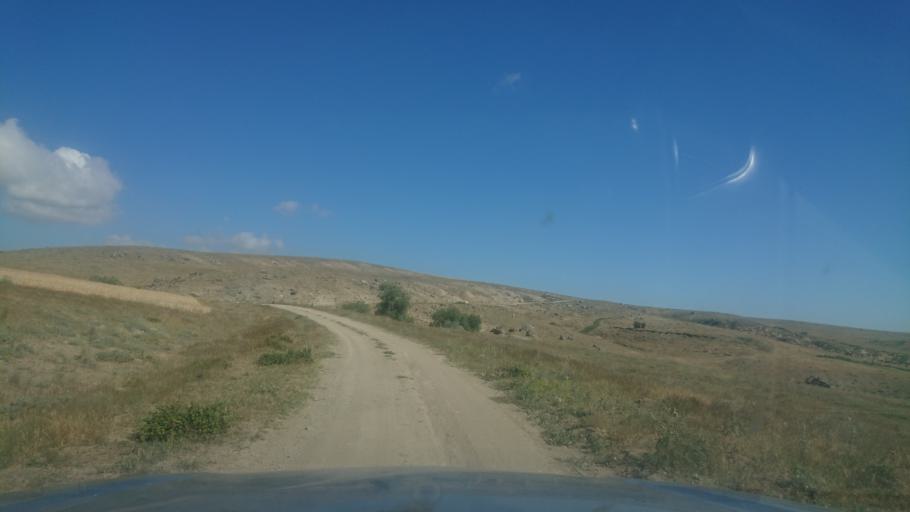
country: TR
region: Aksaray
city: Sariyahsi
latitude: 38.9189
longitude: 33.8542
